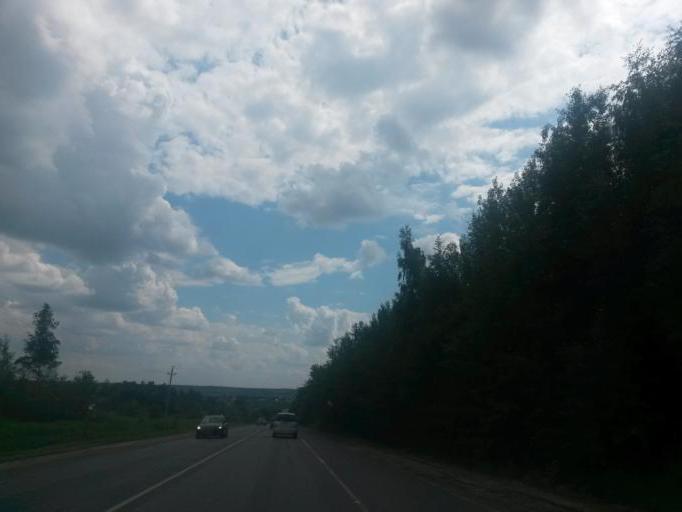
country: RU
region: Moskovskaya
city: Gorki-Leninskiye
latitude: 55.4955
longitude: 37.7803
